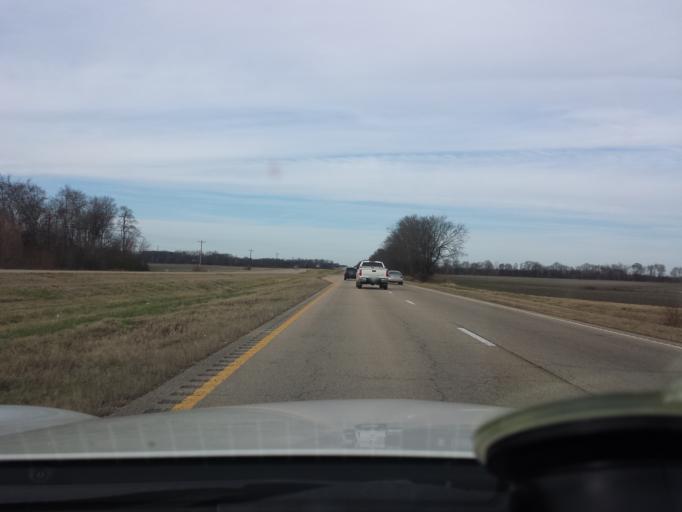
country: US
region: Mississippi
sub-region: Chickasaw County
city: Okolona
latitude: 33.8535
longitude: -88.7152
